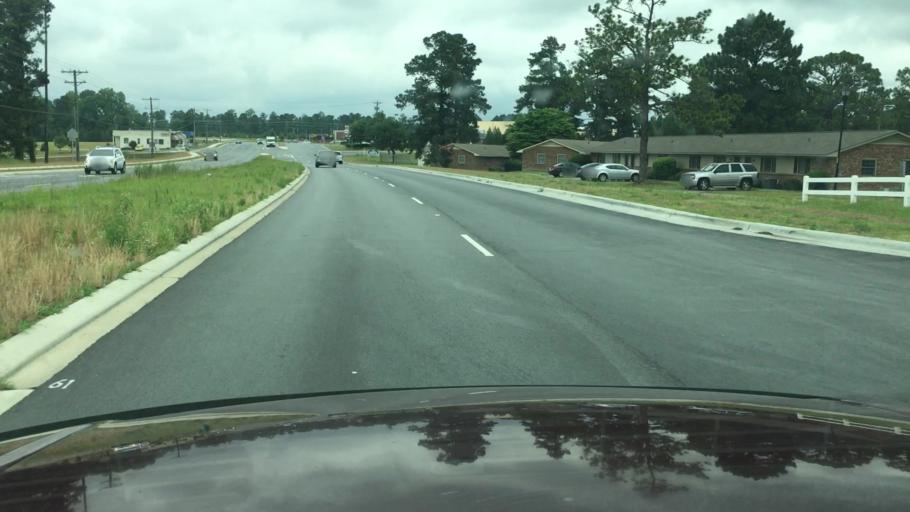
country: US
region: North Carolina
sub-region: Cumberland County
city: Spring Lake
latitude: 35.2514
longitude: -78.9665
